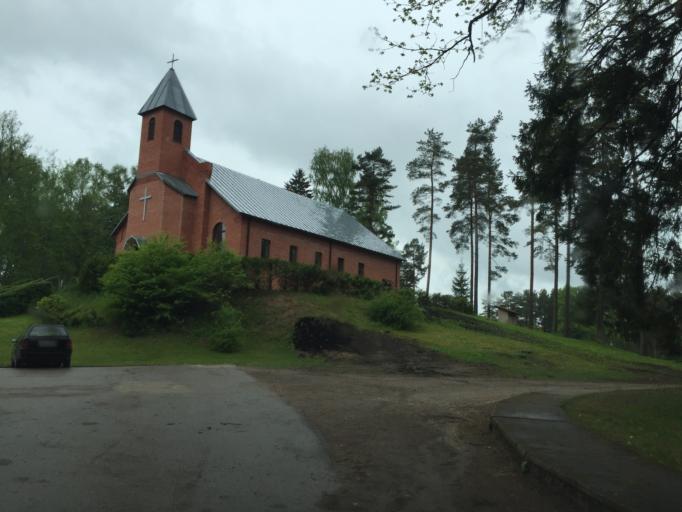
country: LV
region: Lielvarde
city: Lielvarde
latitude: 56.7301
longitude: 24.8047
